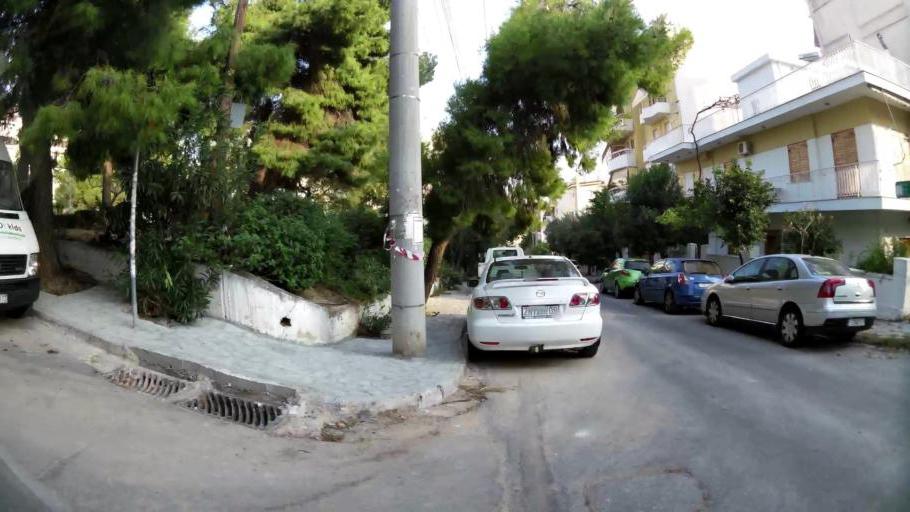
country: GR
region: Attica
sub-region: Nomarchia Athinas
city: Petroupolis
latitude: 38.0466
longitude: 23.6806
